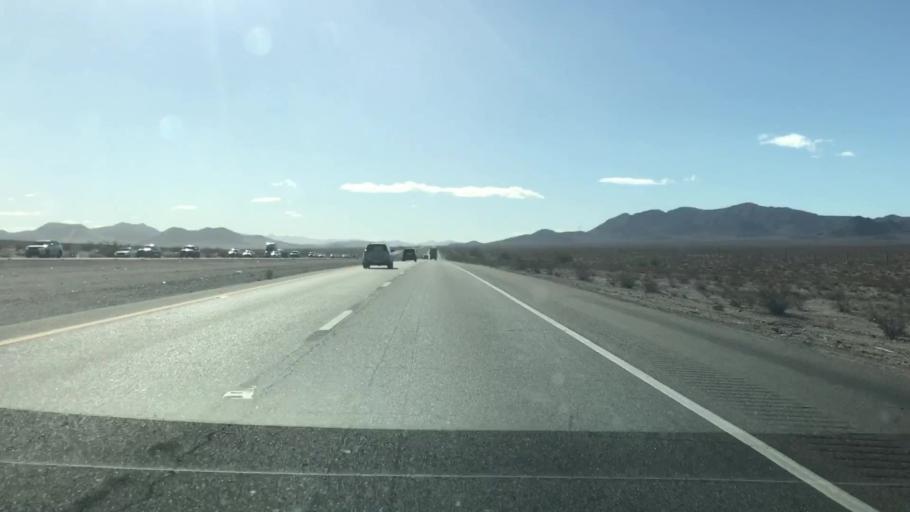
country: US
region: California
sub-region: San Bernardino County
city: Fort Irwin
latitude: 35.1826
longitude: -116.1668
